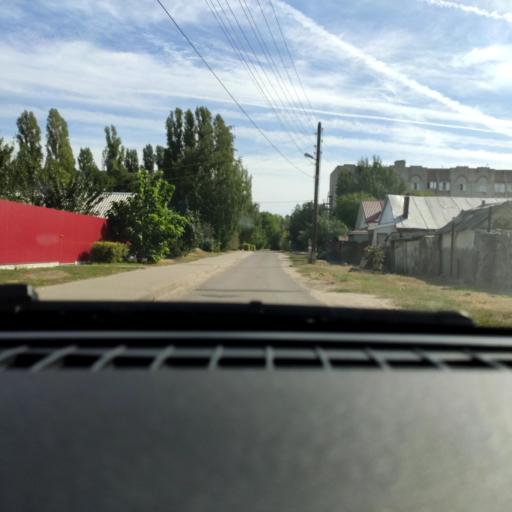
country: RU
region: Voronezj
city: Maslovka
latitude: 51.5511
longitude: 39.2405
